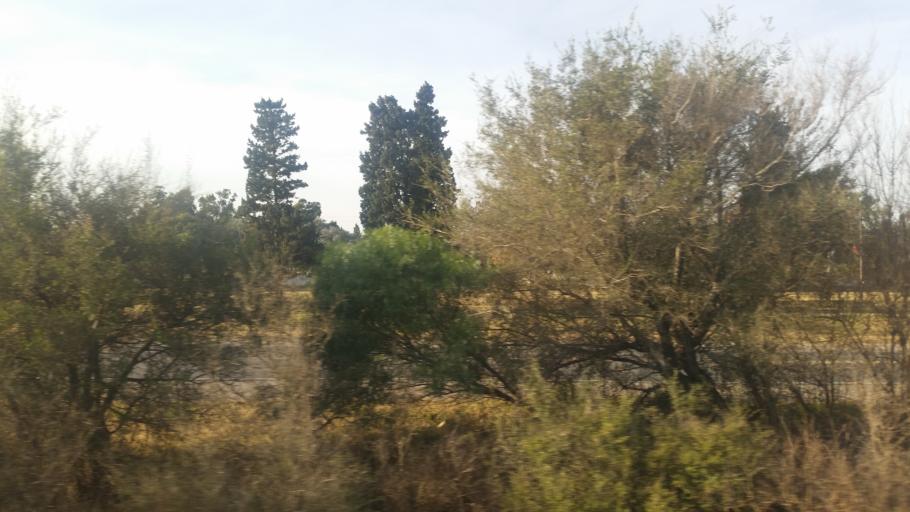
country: AR
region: Cordoba
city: Toledo
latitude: -31.5485
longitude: -64.0173
